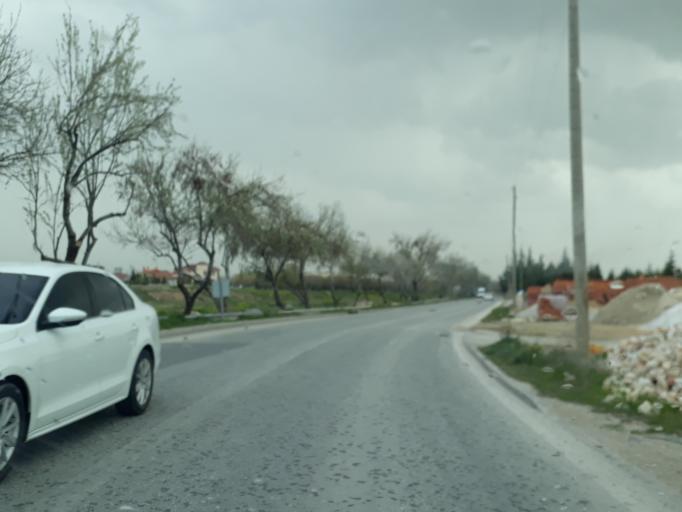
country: TR
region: Konya
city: Selcuklu
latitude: 37.9190
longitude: 32.4713
